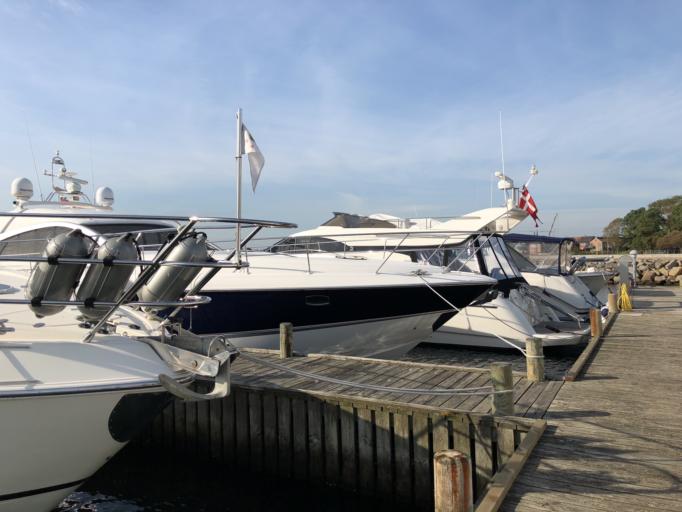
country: DK
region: South Denmark
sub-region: Sonderborg Kommune
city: Sonderborg
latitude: 54.8999
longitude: 9.7924
